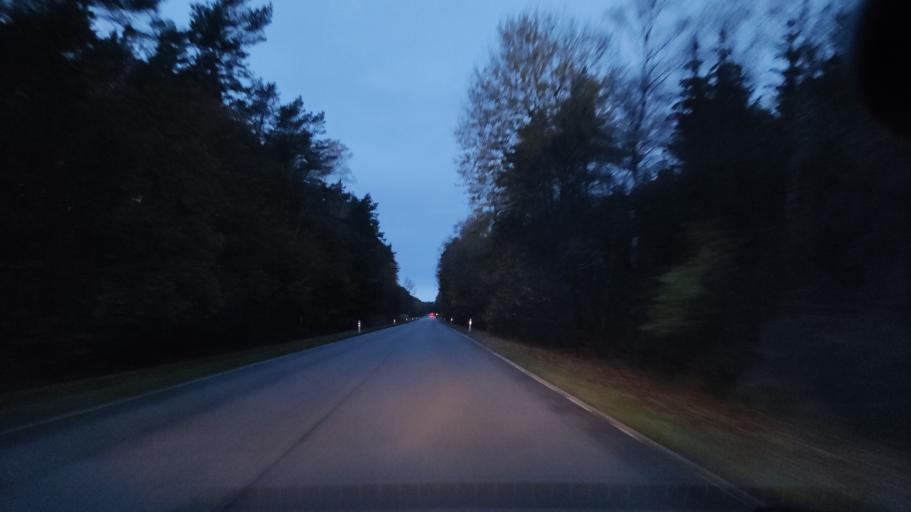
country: DE
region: Lower Saxony
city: Munster
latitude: 53.0172
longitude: 10.0704
